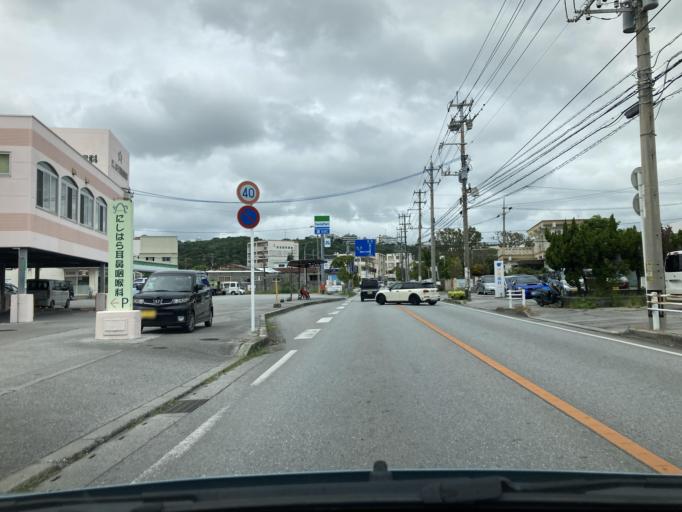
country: JP
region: Okinawa
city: Ginowan
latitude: 26.2269
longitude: 127.7557
